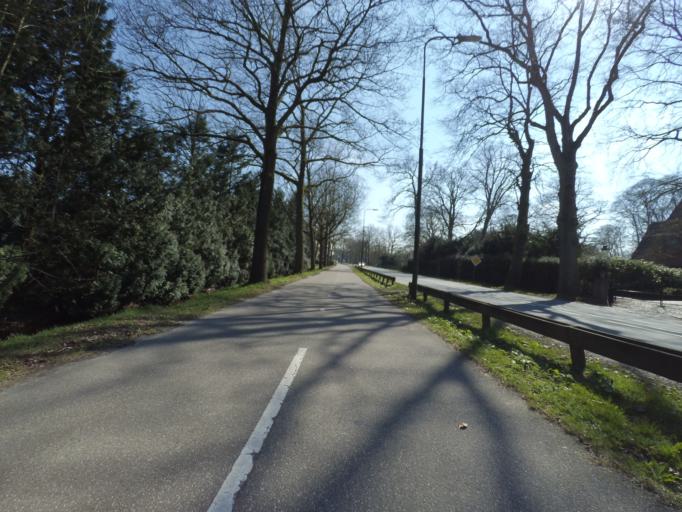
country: NL
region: Utrecht
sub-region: Gemeente Utrechtse Heuvelrug
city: Driebergen-Rijsenburg
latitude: 52.0449
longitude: 5.3007
